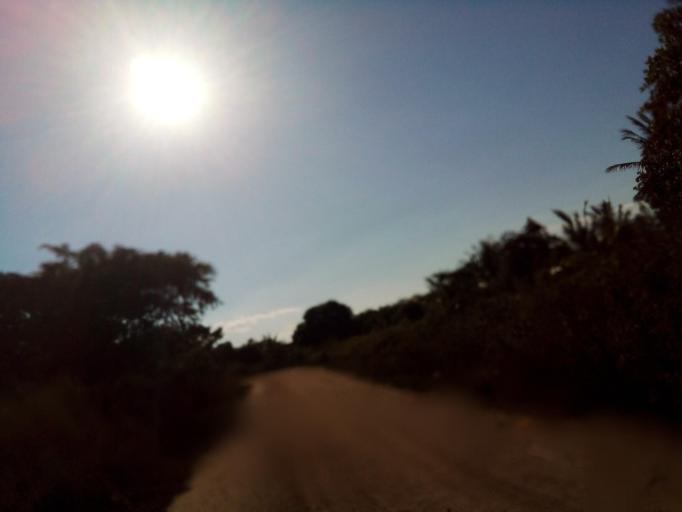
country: MZ
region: Zambezia
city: Quelimane
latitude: -17.4908
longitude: 36.5659
